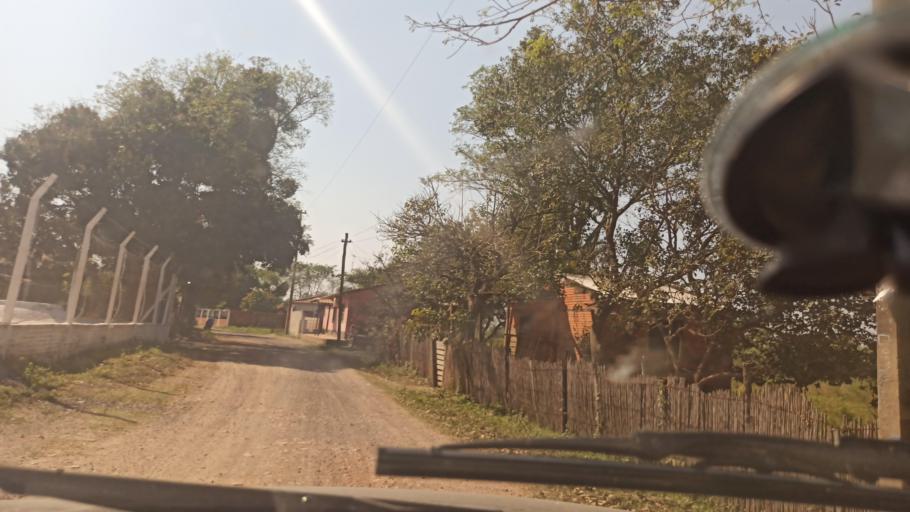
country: AR
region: Formosa
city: Clorinda
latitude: -25.3127
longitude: -57.6980
